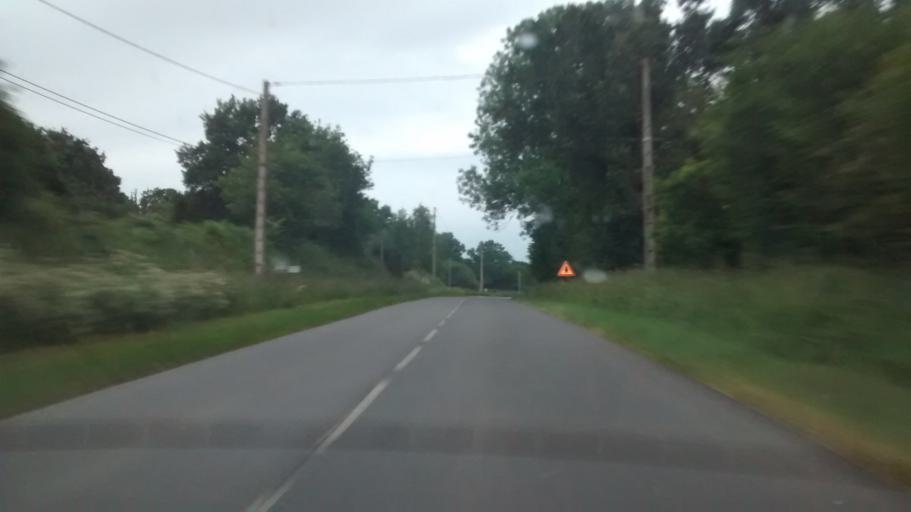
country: FR
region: Brittany
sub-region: Departement du Morbihan
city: Saint-Martin-sur-Oust
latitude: 47.7339
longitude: -2.2782
